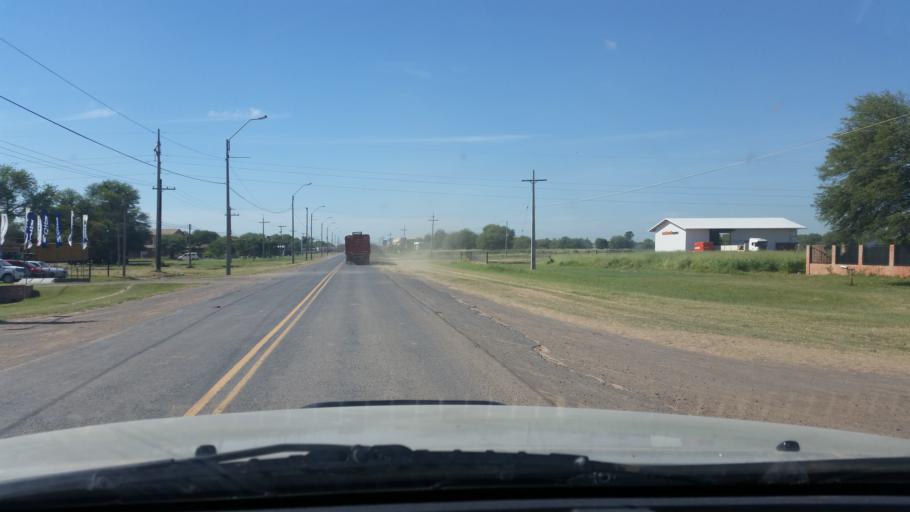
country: PY
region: Boqueron
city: Colonia Menno
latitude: -22.3921
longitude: -59.8365
